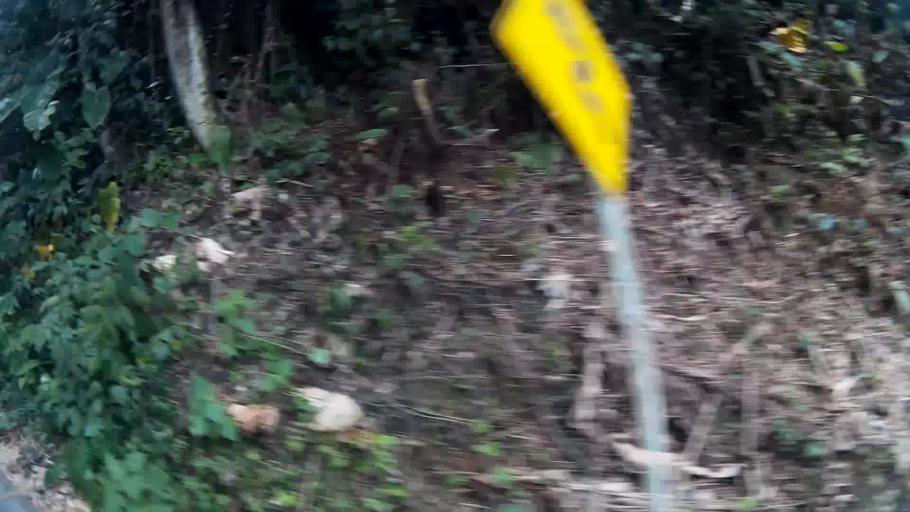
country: CO
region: Risaralda
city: Marsella
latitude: 4.8780
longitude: -75.7608
